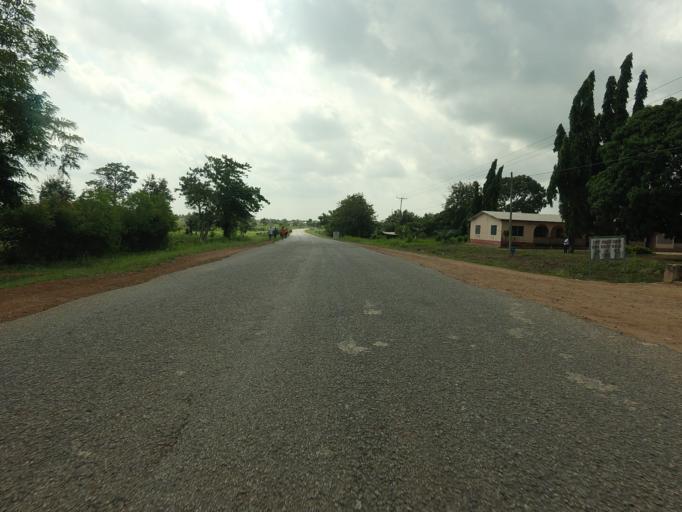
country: GH
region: Volta
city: Ho
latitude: 6.4212
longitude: 0.7376
